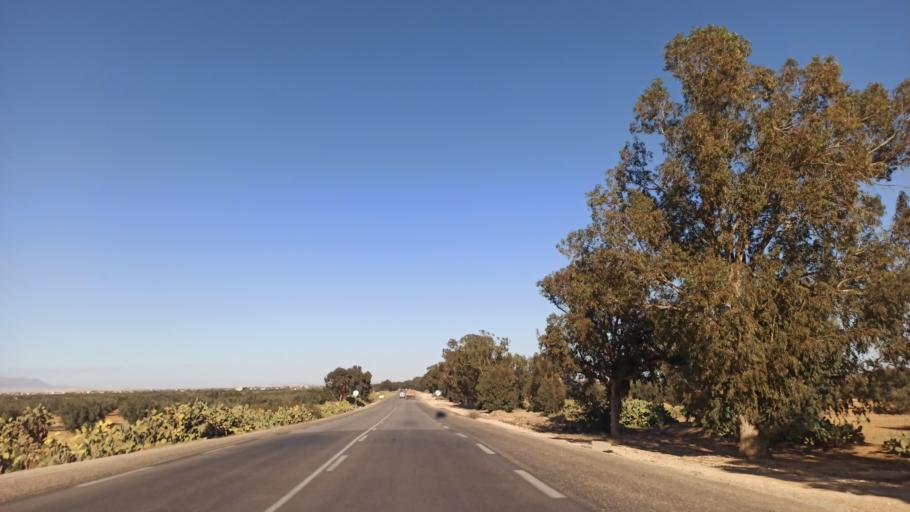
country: TN
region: Sidi Bu Zayd
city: Jilma
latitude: 35.1671
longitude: 9.3692
